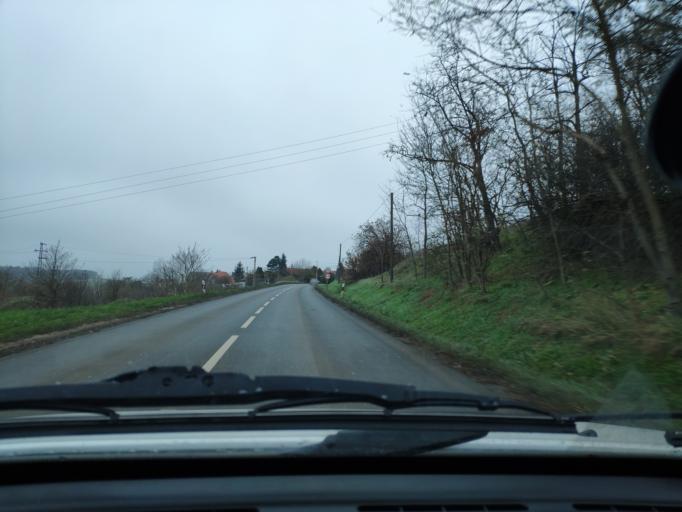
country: HU
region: Pest
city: Biatorbagy
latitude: 47.4558
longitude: 18.8142
